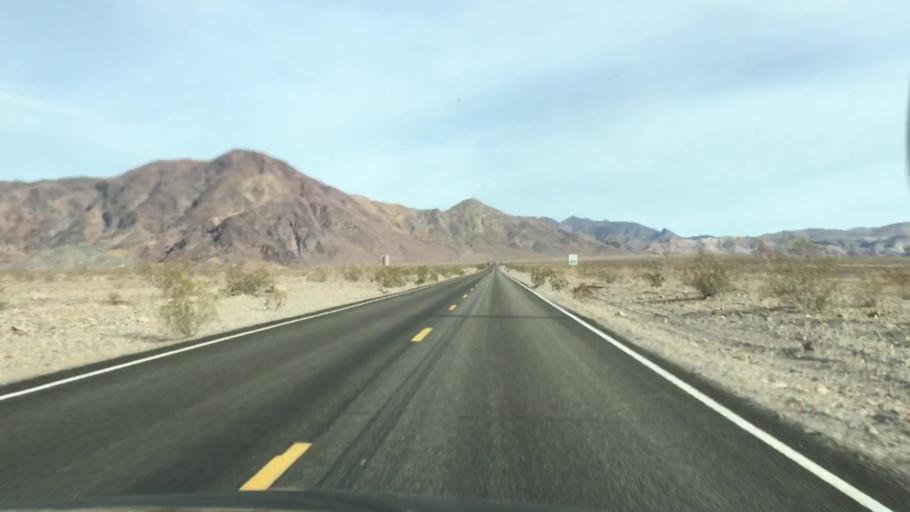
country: US
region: Nevada
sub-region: Nye County
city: Beatty
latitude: 36.6801
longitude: -117.0085
